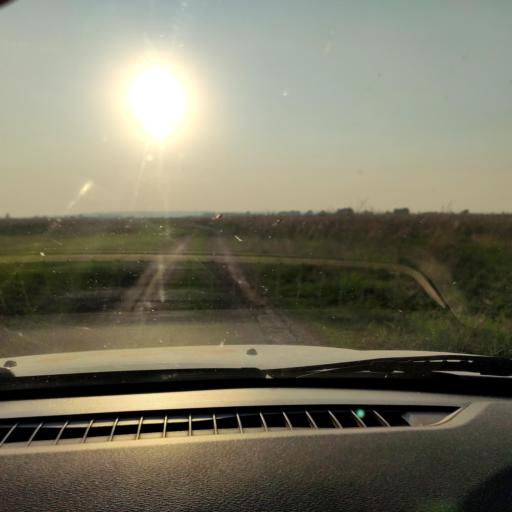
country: RU
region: Bashkortostan
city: Mikhaylovka
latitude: 54.9529
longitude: 55.8182
